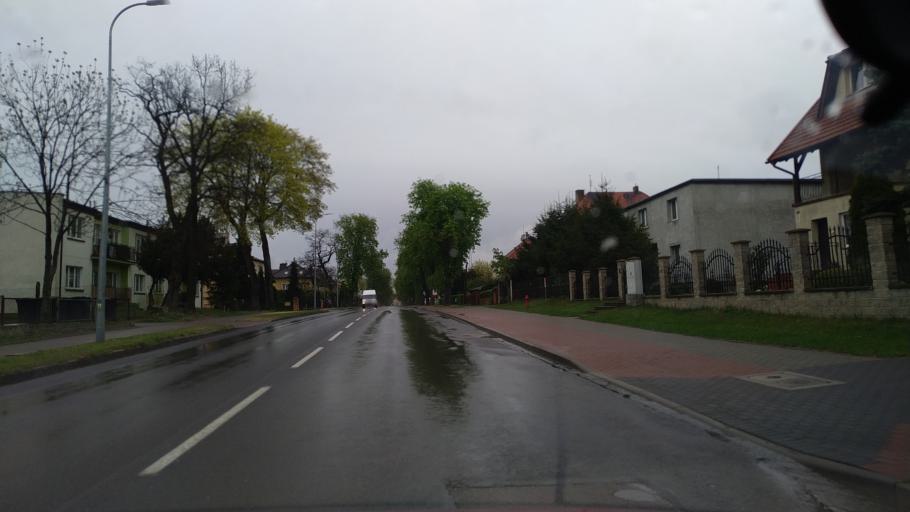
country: PL
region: Pomeranian Voivodeship
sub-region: Powiat czluchowski
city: Czluchow
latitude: 53.6700
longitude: 17.3648
